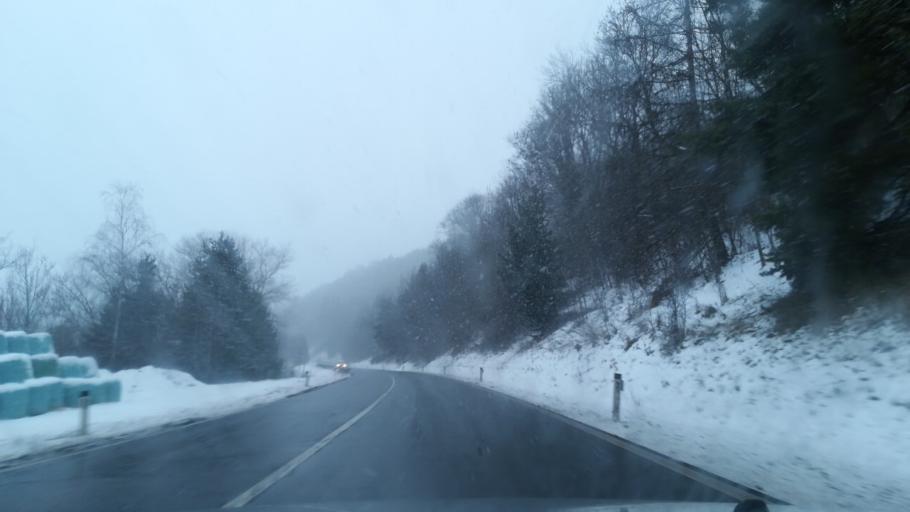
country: AT
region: Styria
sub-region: Politischer Bezirk Murtal
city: Poels
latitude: 47.2046
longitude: 14.5853
